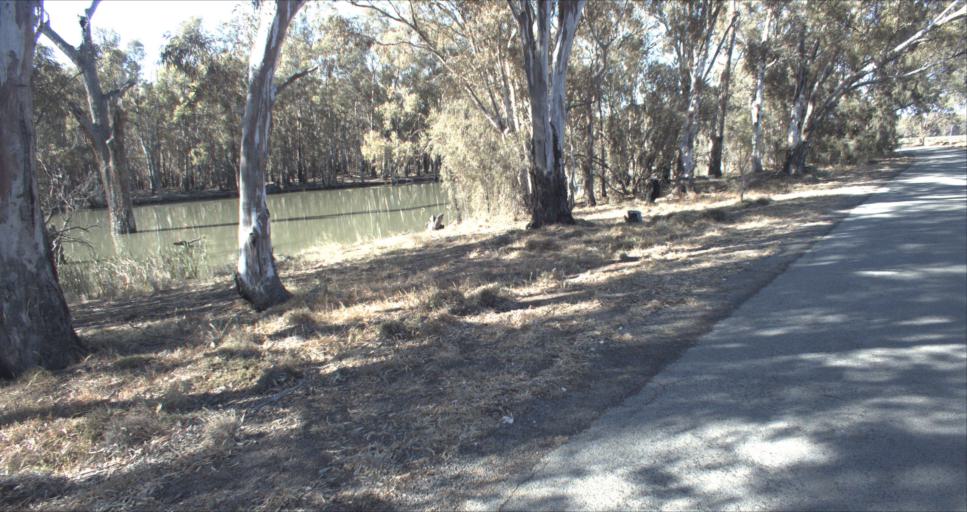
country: AU
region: New South Wales
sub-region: Leeton
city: Leeton
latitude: -34.6093
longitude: 146.2610
